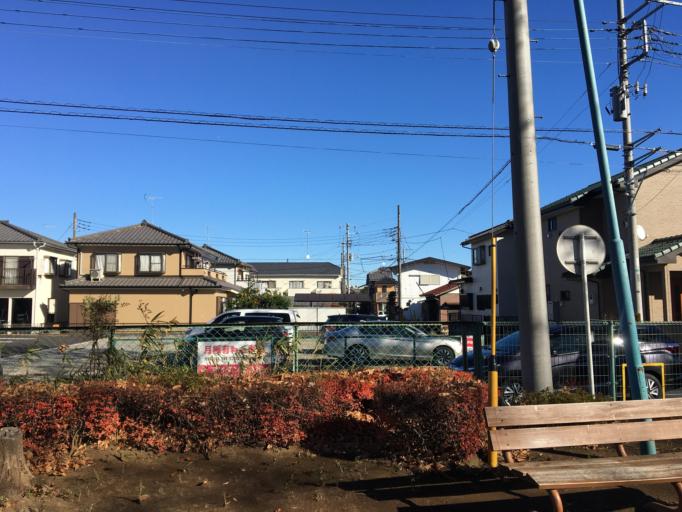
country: JP
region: Saitama
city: Sakado
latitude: 35.9384
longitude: 139.4161
